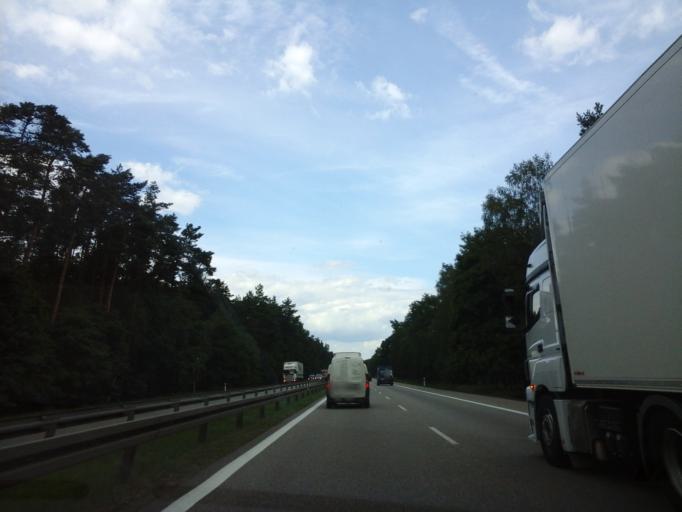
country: PL
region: West Pomeranian Voivodeship
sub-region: Powiat goleniowski
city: Goleniow
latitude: 53.4477
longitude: 14.7838
